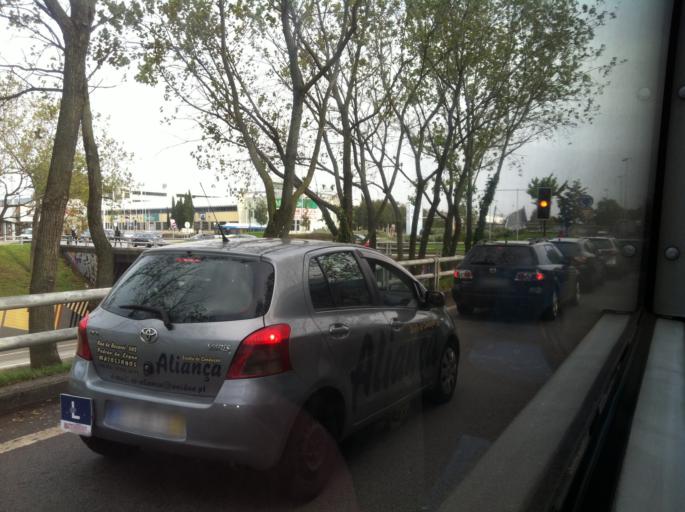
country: PT
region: Porto
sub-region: Matosinhos
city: Senhora da Hora
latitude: 41.1784
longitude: -8.6563
